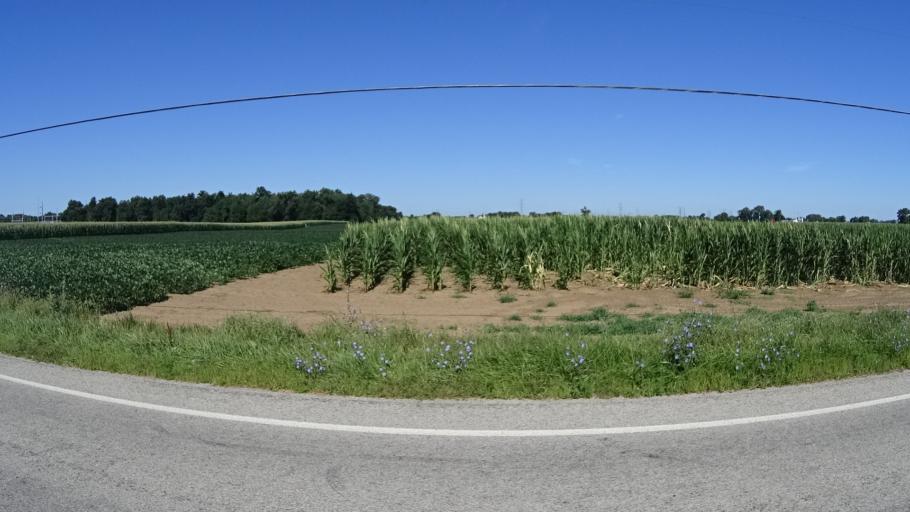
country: US
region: Ohio
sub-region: Erie County
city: Sandusky
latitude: 41.3791
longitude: -82.7236
